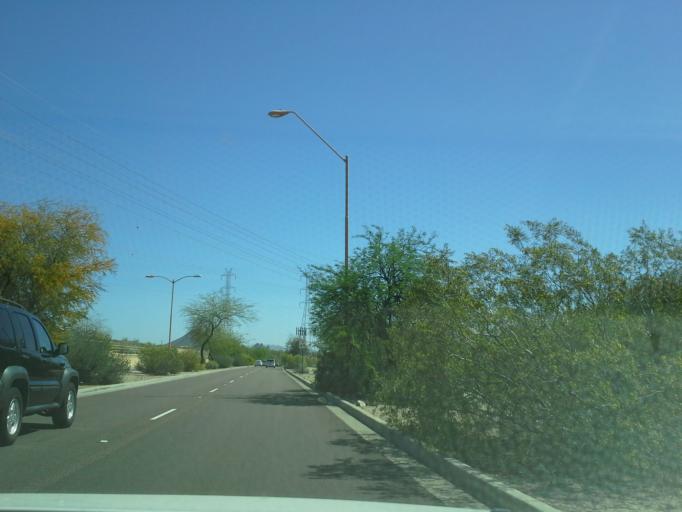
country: US
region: Arizona
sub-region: Maricopa County
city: Scottsdale
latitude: 33.5997
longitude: -111.8470
